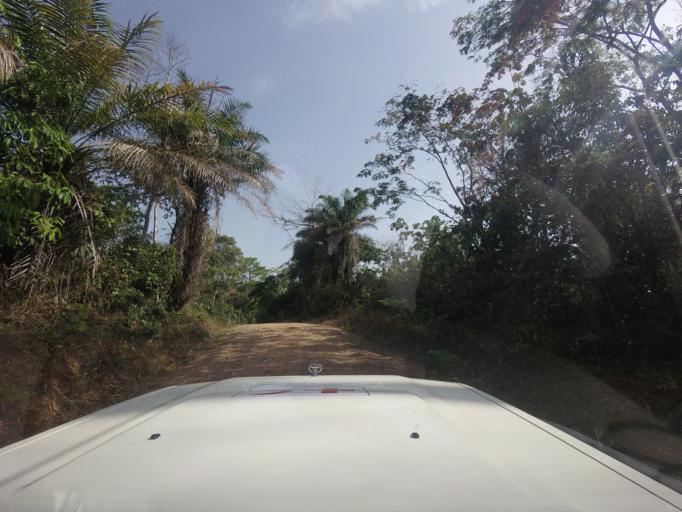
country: LR
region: Lofa
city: Voinjama
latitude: 8.4762
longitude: -9.7611
